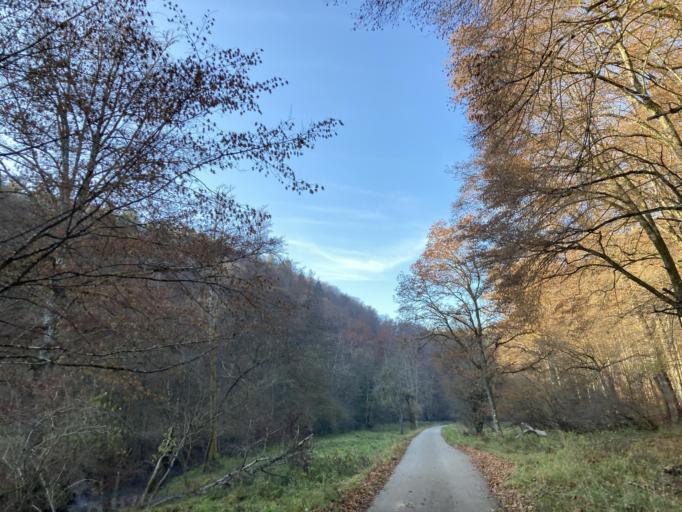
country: DE
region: Baden-Wuerttemberg
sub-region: Tuebingen Region
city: Tuebingen
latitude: 48.5630
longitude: 9.0364
